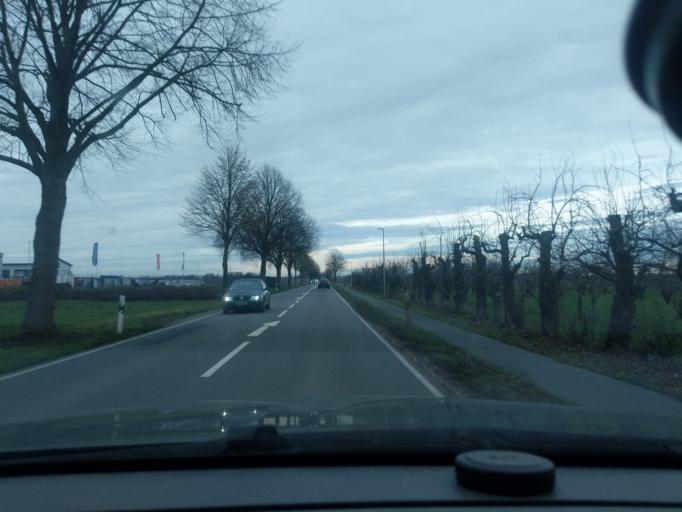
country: DE
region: Lower Saxony
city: Beckdorf
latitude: 53.4193
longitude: 9.6117
